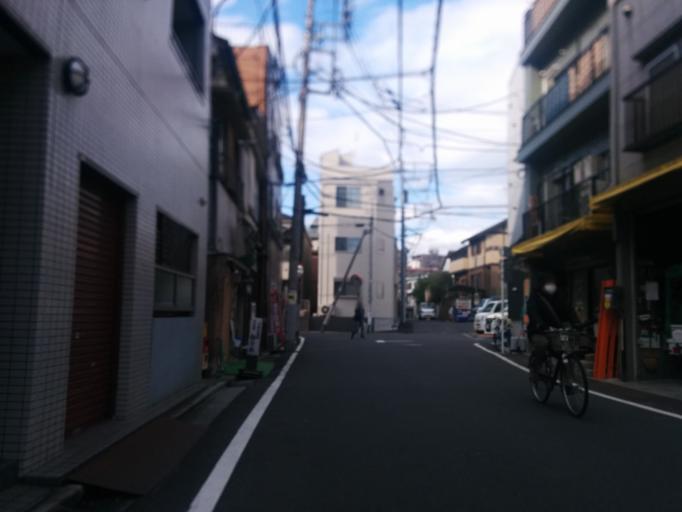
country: JP
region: Tokyo
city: Tokyo
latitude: 35.7171
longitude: 139.7532
